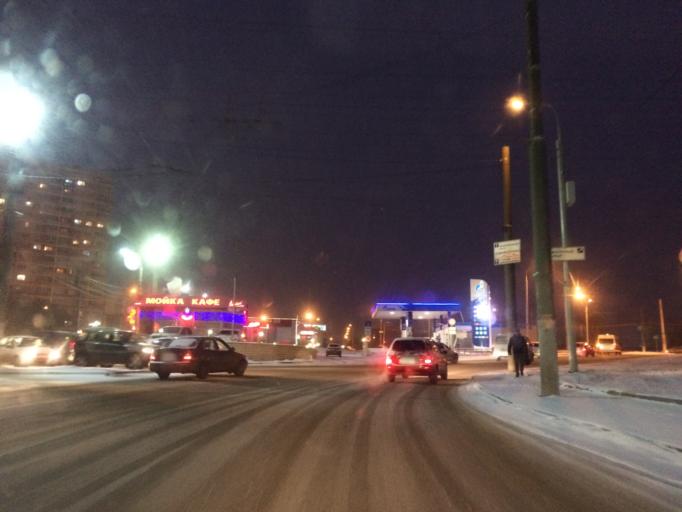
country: RU
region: Tula
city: Tula
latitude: 54.1967
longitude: 37.6599
